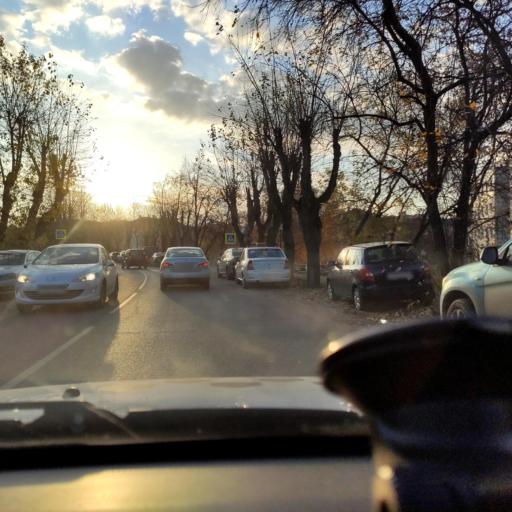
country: RU
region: Perm
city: Perm
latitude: 58.0072
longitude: 56.1974
